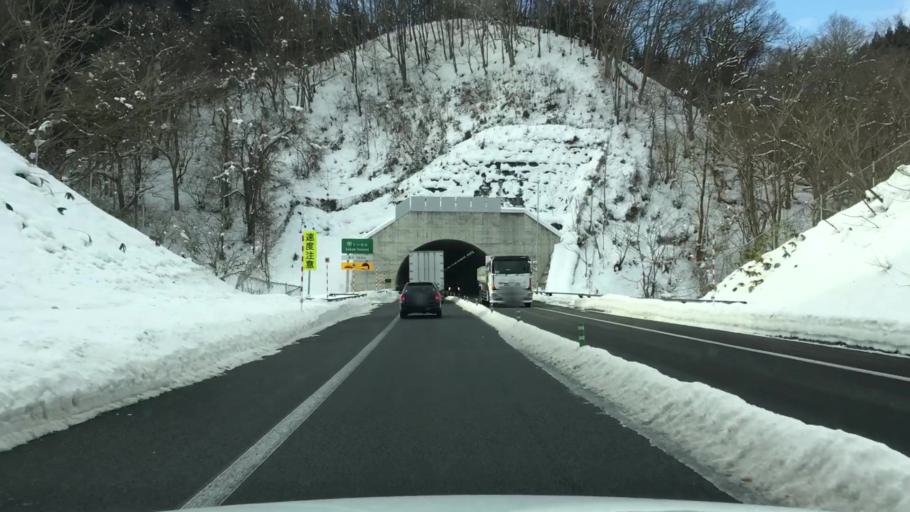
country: JP
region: Akita
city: Takanosu
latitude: 40.2231
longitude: 140.4319
